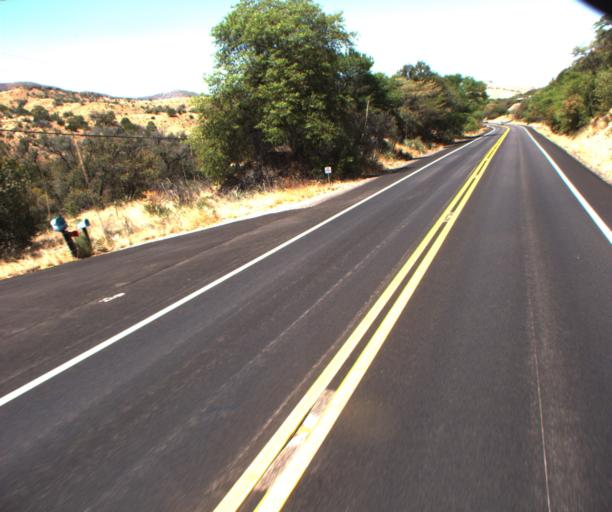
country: US
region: Arizona
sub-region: Cochise County
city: Bisbee
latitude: 31.4811
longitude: -109.9809
